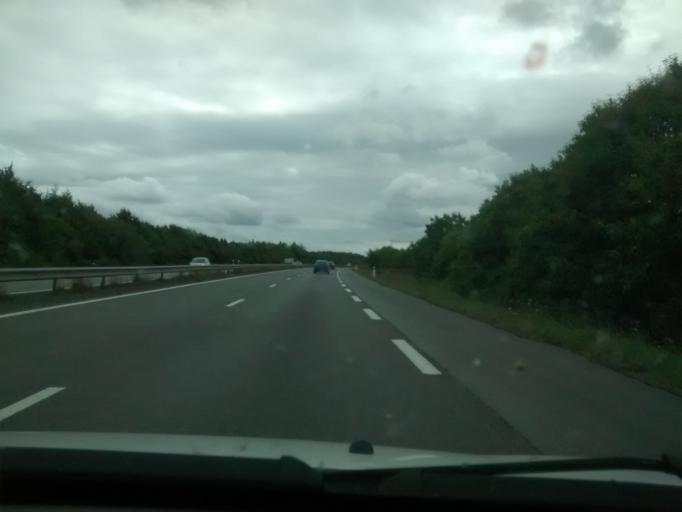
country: FR
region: Brittany
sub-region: Departement d'Ille-et-Vilaine
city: Saint-Domineuc
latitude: 48.3494
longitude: -1.8635
